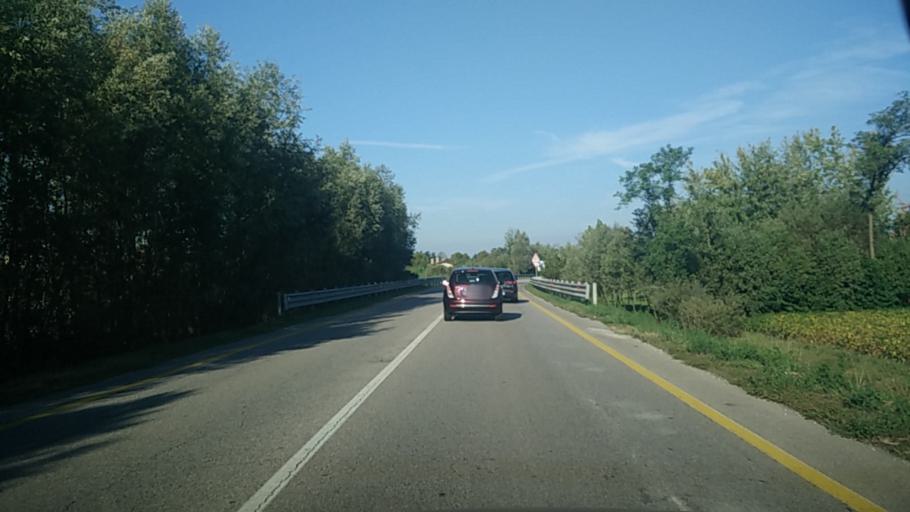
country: IT
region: Veneto
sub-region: Provincia di Padova
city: Piombino Dese
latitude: 45.6158
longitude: 11.9947
